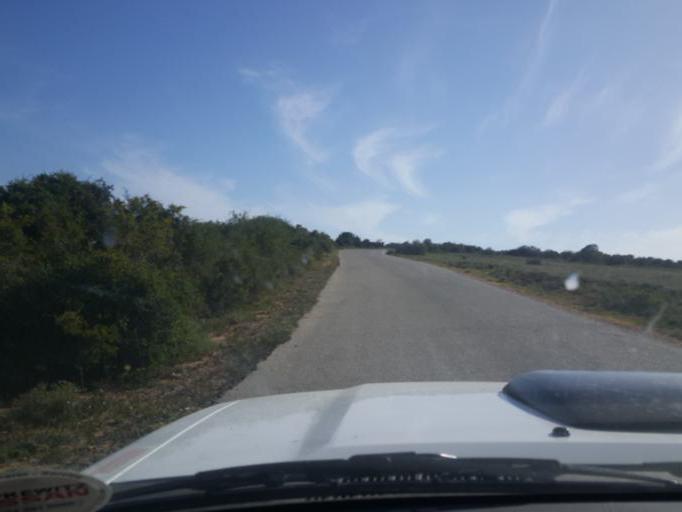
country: ZA
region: Eastern Cape
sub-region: Cacadu District Municipality
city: Kirkwood
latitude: -33.4381
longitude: 25.7832
